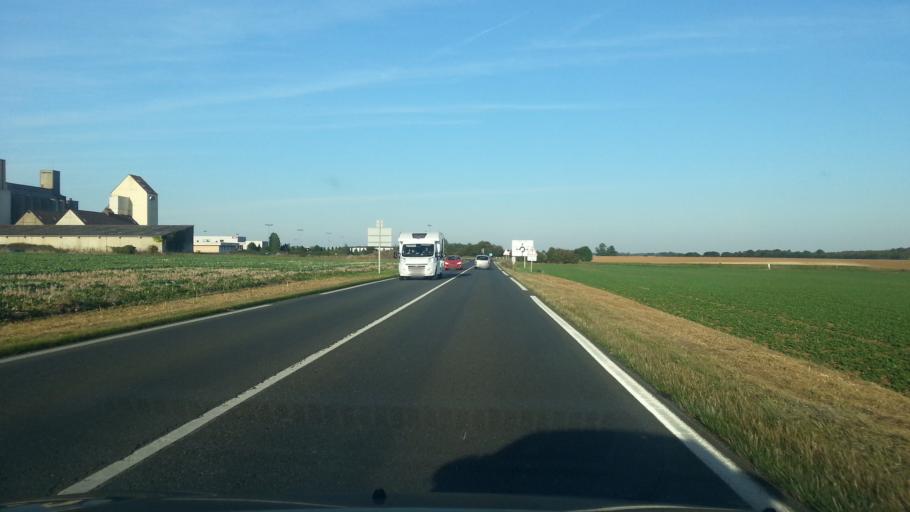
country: FR
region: Picardie
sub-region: Departement de l'Oise
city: Sacy-le-Grand
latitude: 49.3873
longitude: 2.5751
